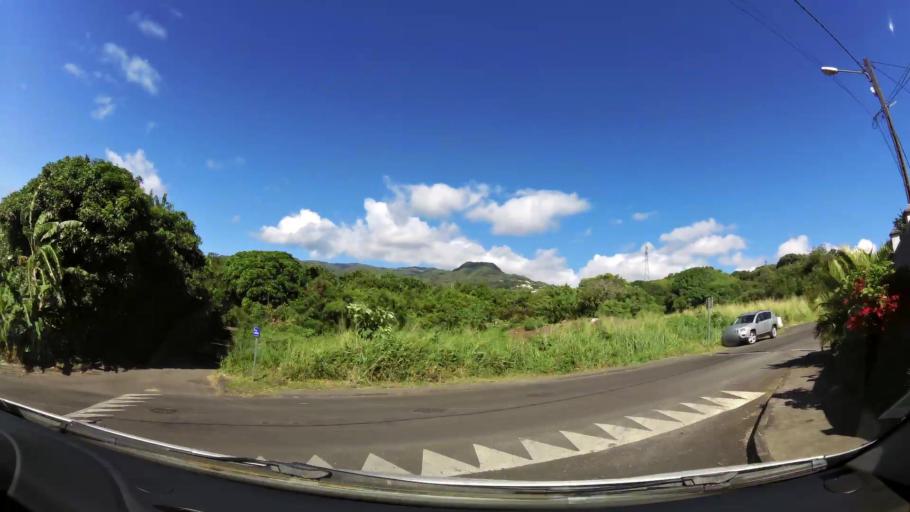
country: RE
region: Reunion
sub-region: Reunion
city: Saint-Denis
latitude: -20.9192
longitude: 55.4827
